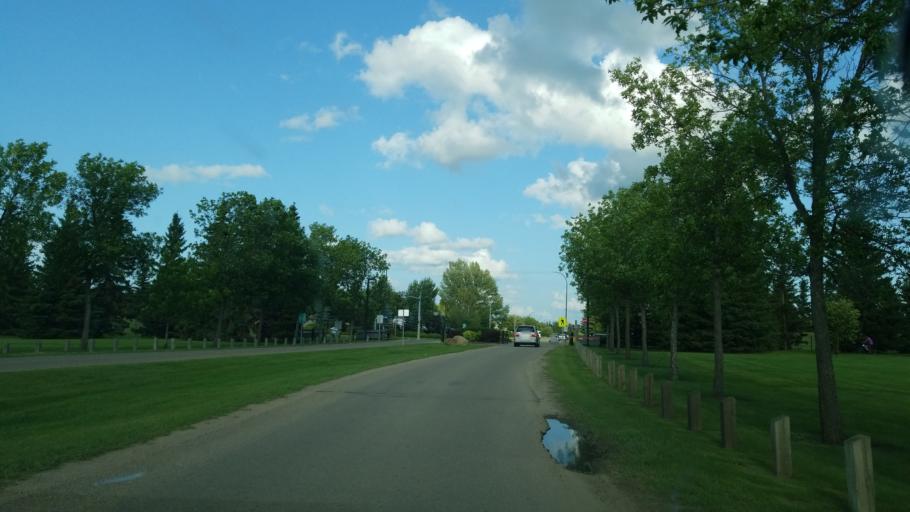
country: CA
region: Saskatchewan
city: Lloydminster
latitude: 53.2638
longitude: -110.0313
